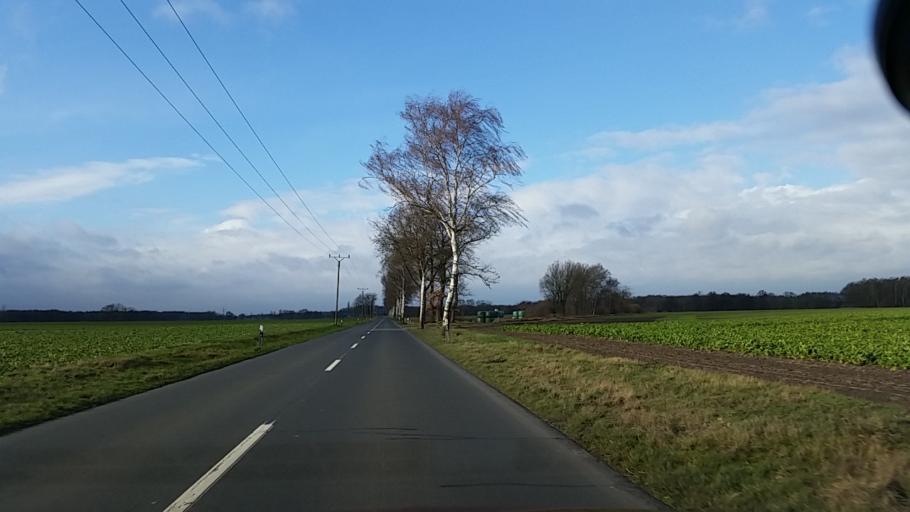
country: DE
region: Lower Saxony
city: Wrestedt
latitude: 52.9060
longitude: 10.5628
